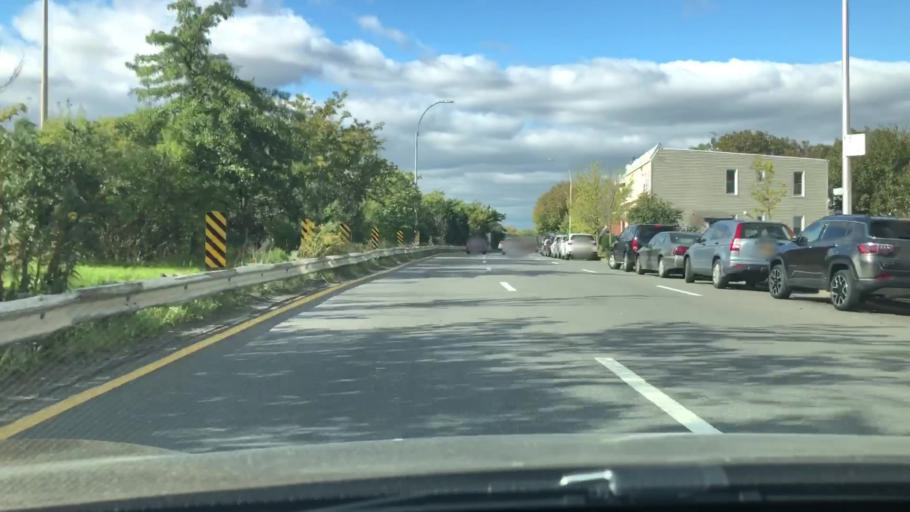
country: US
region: New York
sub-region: Kings County
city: East New York
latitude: 40.7259
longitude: -73.8915
